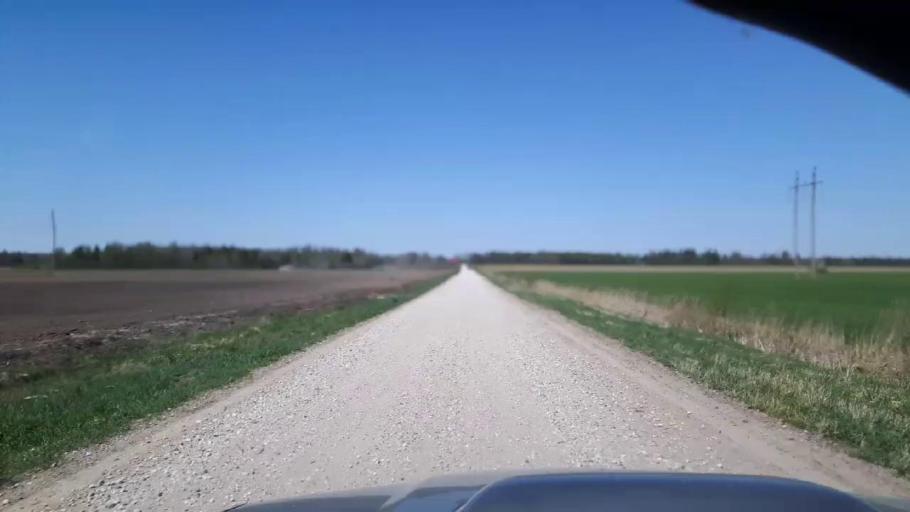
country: EE
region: Paernumaa
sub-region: Sindi linn
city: Sindi
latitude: 58.4768
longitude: 24.7457
